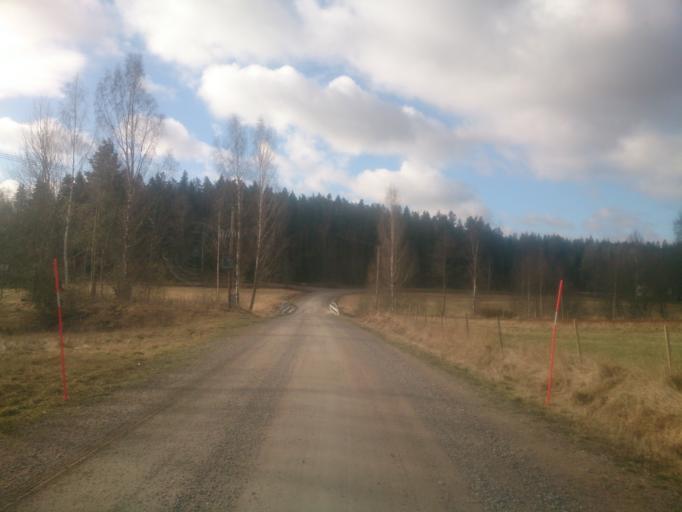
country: SE
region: OEstergoetland
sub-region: Atvidabergs Kommun
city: Atvidaberg
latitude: 58.2094
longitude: 16.1670
